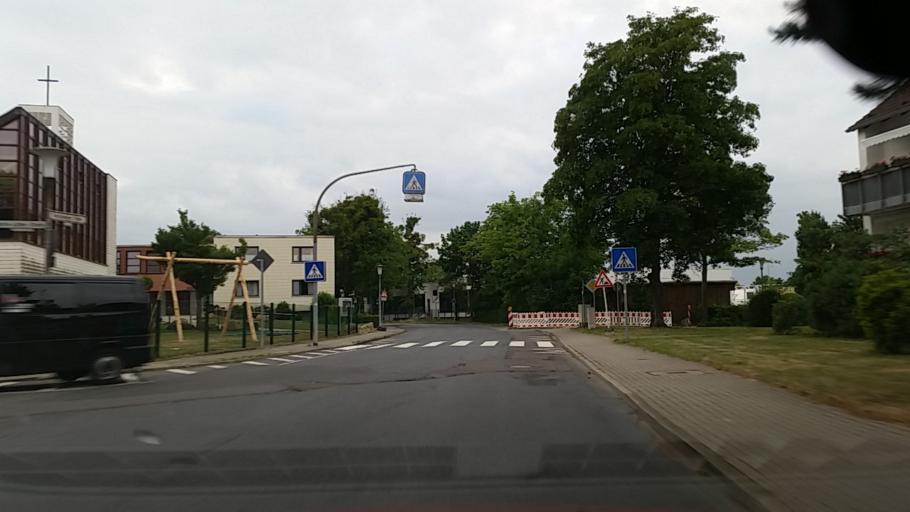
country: DE
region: Lower Saxony
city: Wolfsburg
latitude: 52.4244
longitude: 10.7654
